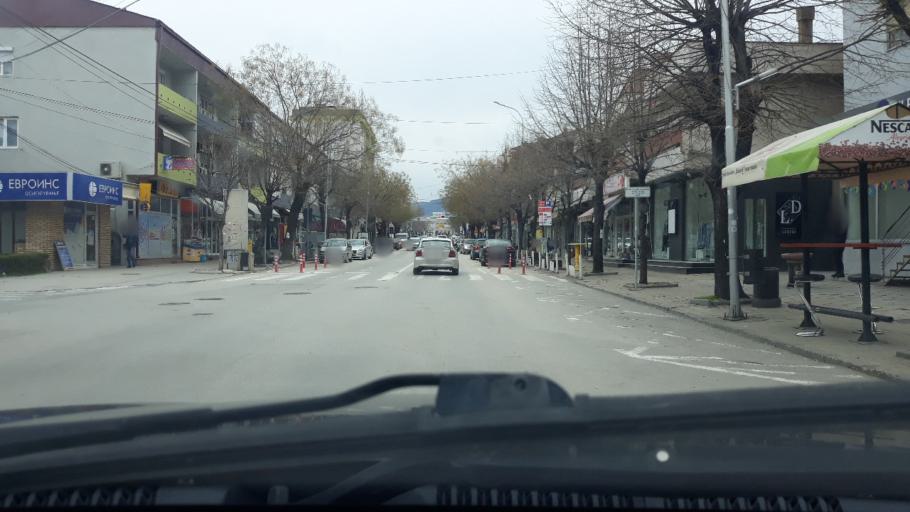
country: MK
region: Kavadarci
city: Kavadarci
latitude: 41.4364
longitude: 22.0110
